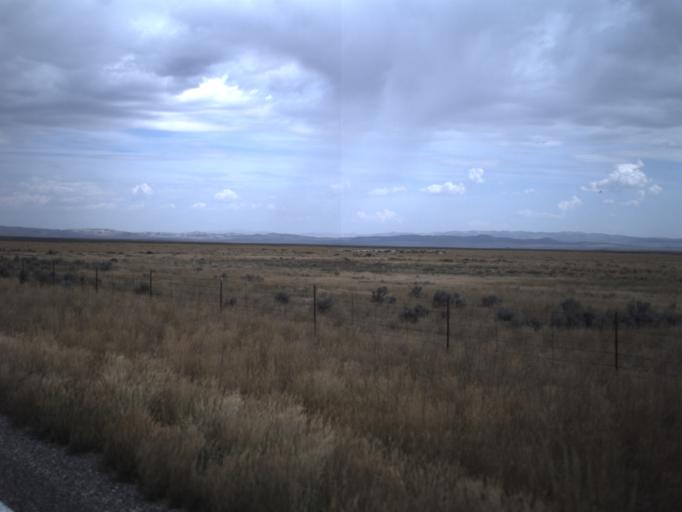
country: US
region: Idaho
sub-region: Oneida County
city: Malad City
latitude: 41.9138
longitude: -113.0991
